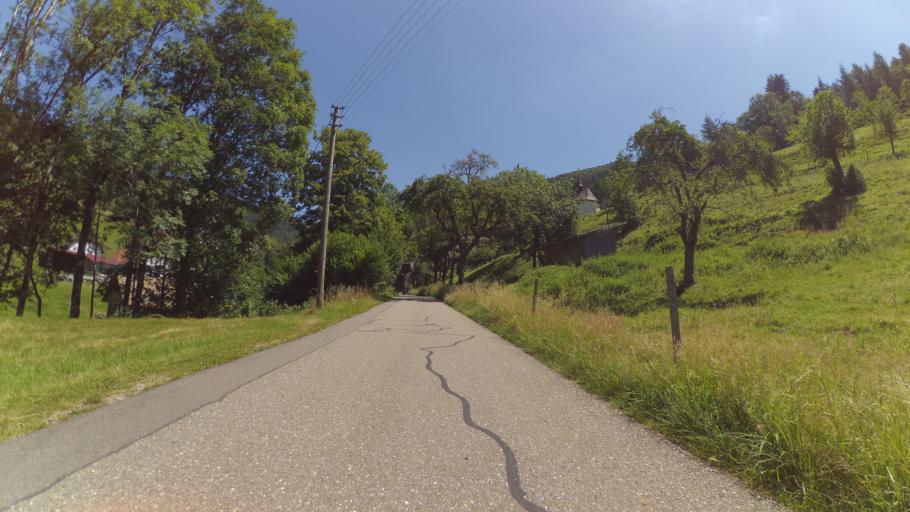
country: DE
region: Baden-Wuerttemberg
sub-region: Freiburg Region
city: Elzach
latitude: 48.1124
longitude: 8.0772
